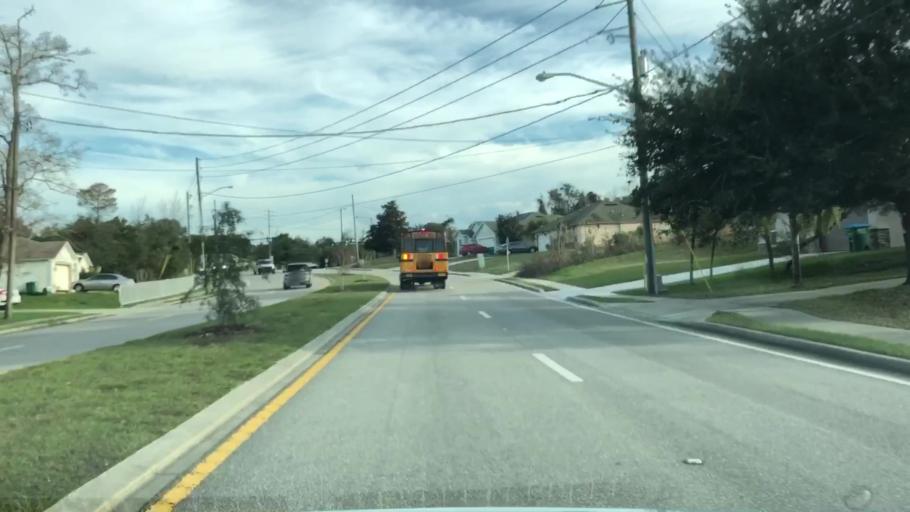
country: US
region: Florida
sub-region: Volusia County
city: Deltona
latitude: 28.9250
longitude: -81.2590
